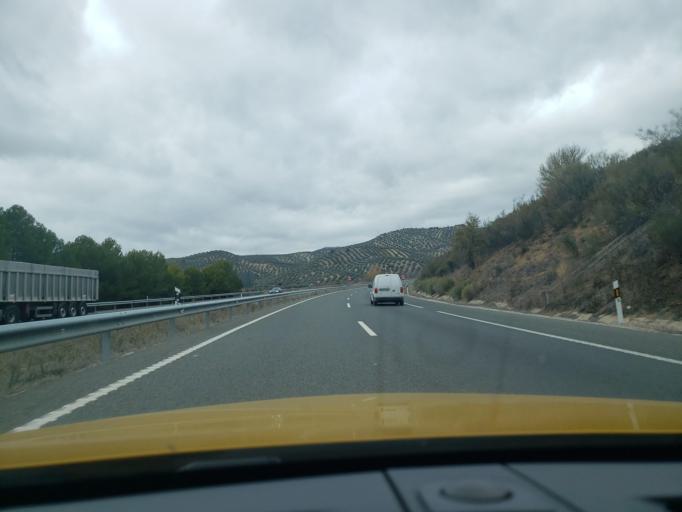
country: ES
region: Andalusia
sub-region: Provincia de Granada
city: Campotejar
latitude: 37.4895
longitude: -3.6192
